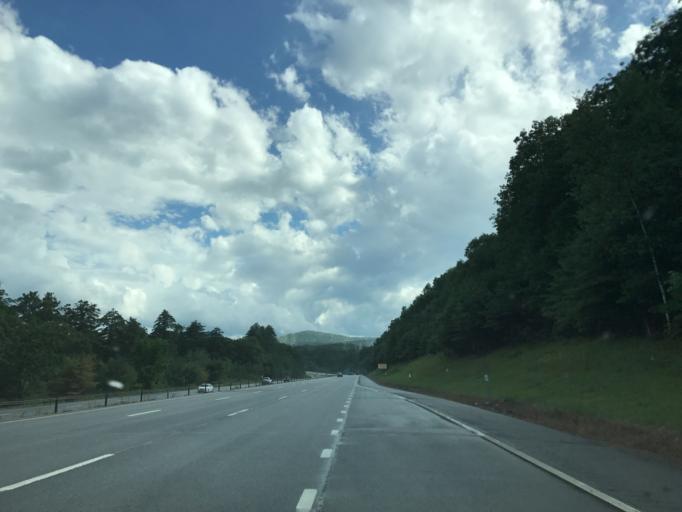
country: US
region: New York
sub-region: Warren County
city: Warrensburg
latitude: 43.4213
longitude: -73.7221
